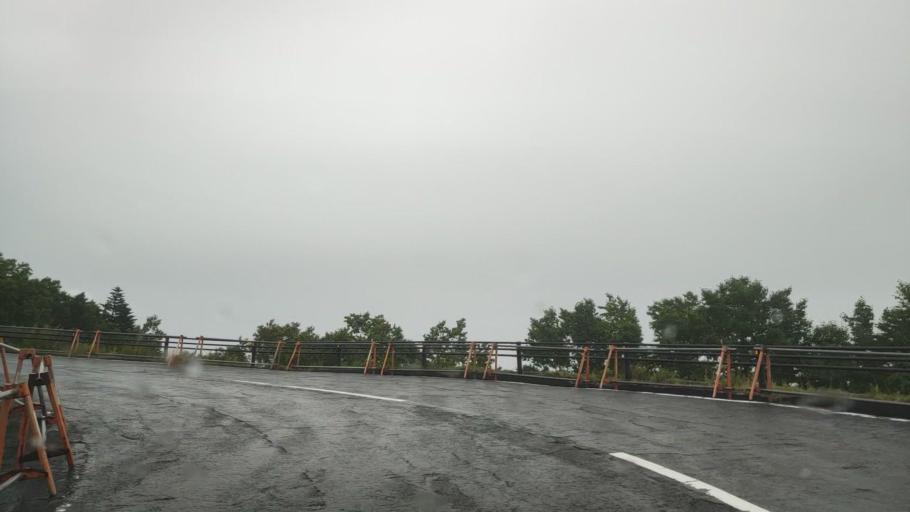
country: JP
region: Shizuoka
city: Fujinomiya
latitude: 35.3310
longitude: 138.7345
